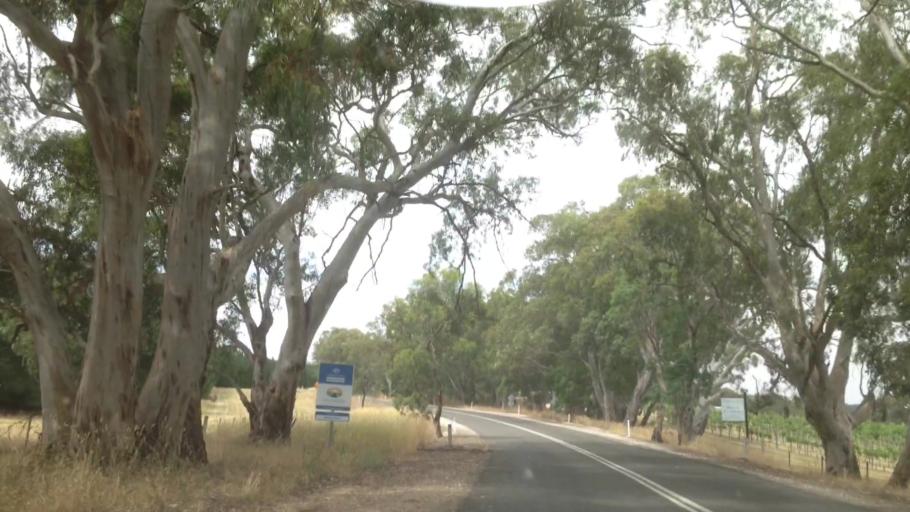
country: AU
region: South Australia
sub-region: Barossa
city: Williamstown
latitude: -34.6878
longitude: 138.9708
